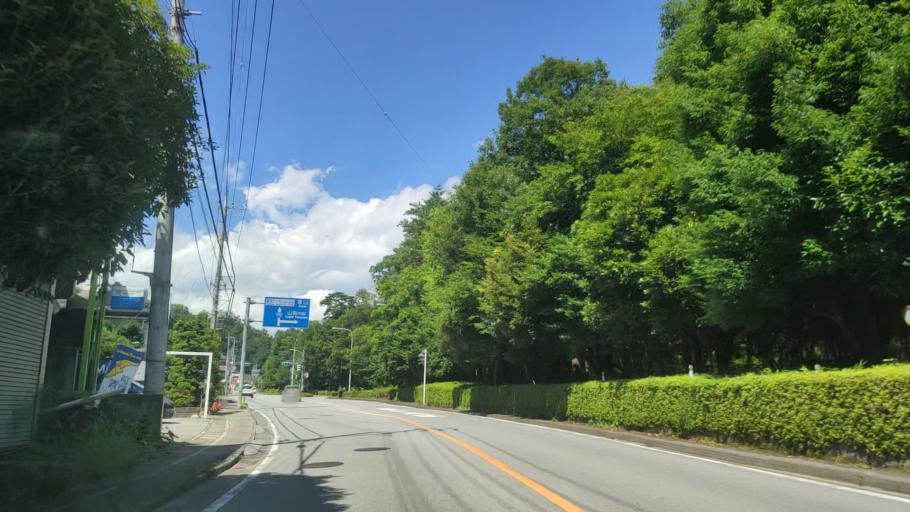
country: JP
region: Yamanashi
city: Enzan
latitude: 35.6914
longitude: 138.6804
